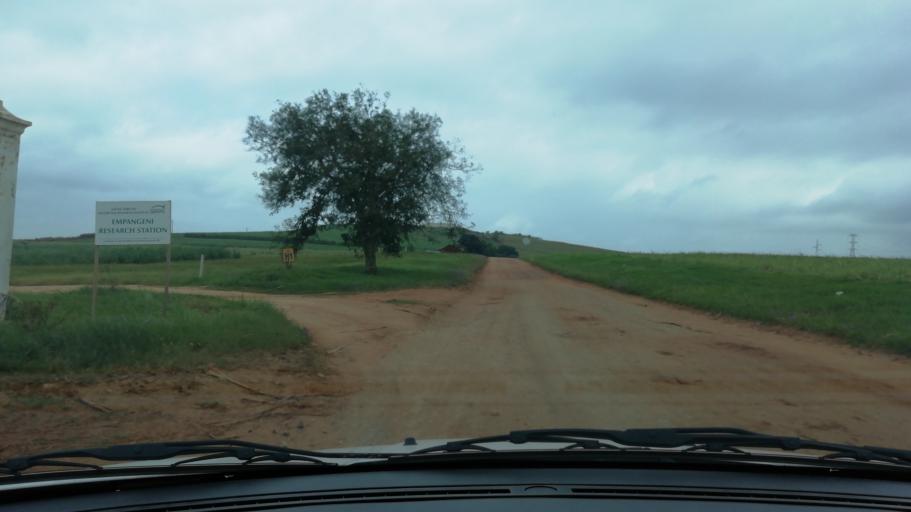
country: ZA
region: KwaZulu-Natal
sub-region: uThungulu District Municipality
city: Empangeni
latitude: -28.7309
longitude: 31.9024
